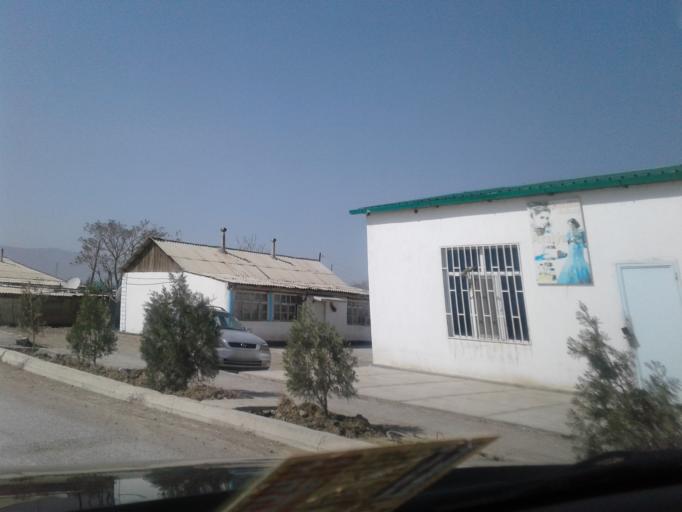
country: TM
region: Ahal
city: Abadan
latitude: 38.1612
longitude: 57.9800
